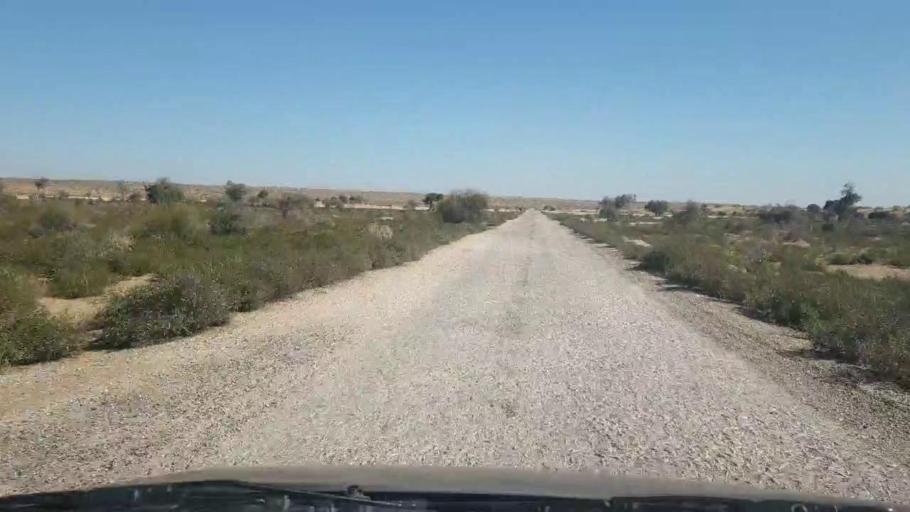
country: PK
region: Sindh
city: Bozdar
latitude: 27.0182
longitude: 68.7643
